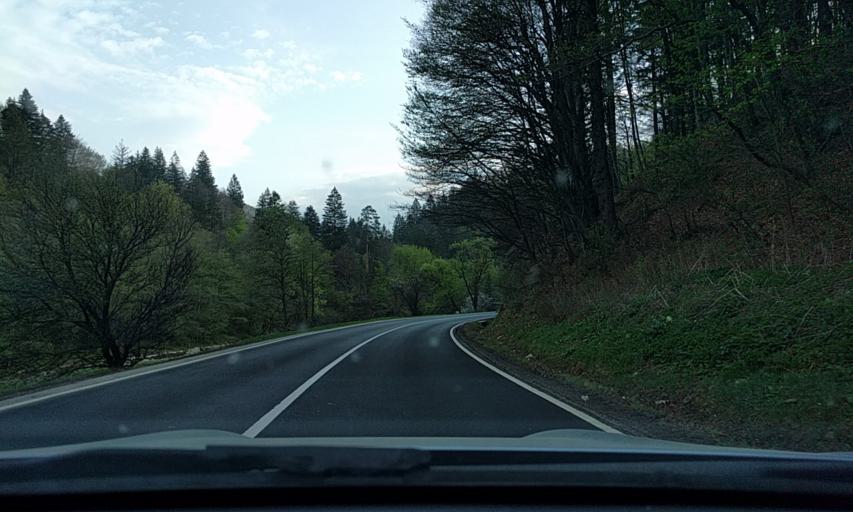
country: RO
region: Covasna
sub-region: Comuna Bretcu
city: Bretcu
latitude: 46.0790
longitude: 26.3958
